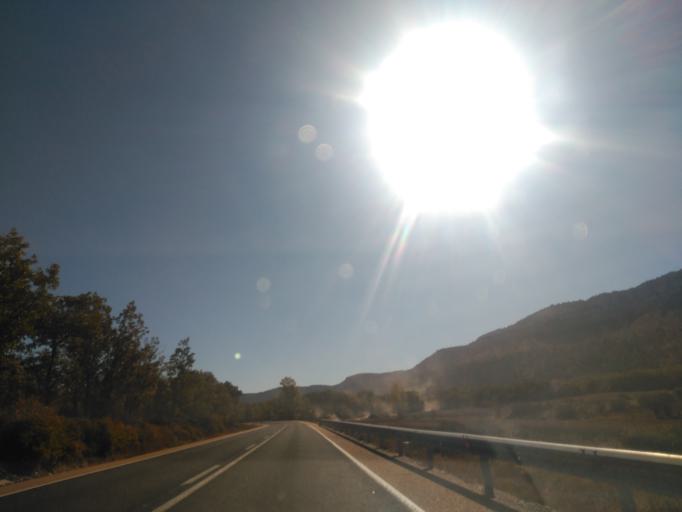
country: ES
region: Castille and Leon
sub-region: Provincia de Soria
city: Cidones
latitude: 41.8120
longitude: -2.7047
